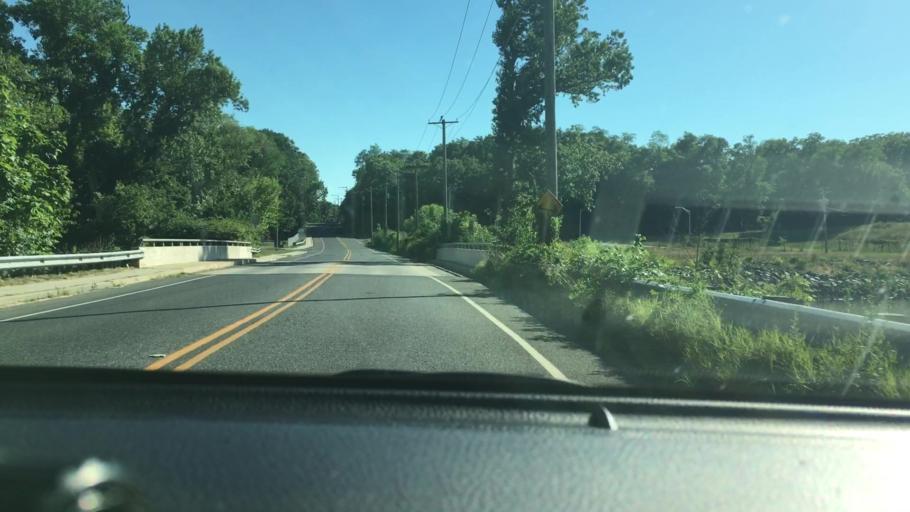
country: US
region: New Jersey
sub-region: Cumberland County
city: Millville
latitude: 39.4008
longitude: -75.0531
